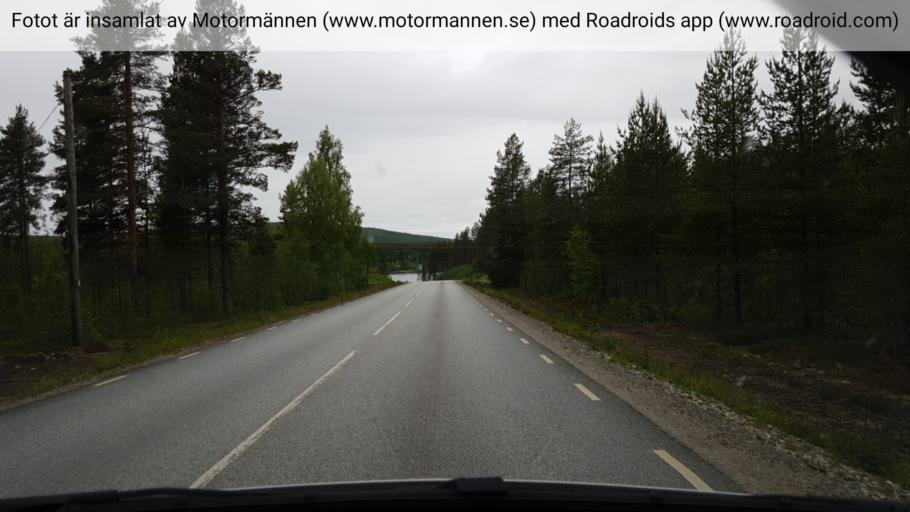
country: SE
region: Vaesterbotten
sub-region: Vindelns Kommun
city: Vindeln
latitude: 64.2038
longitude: 19.4287
